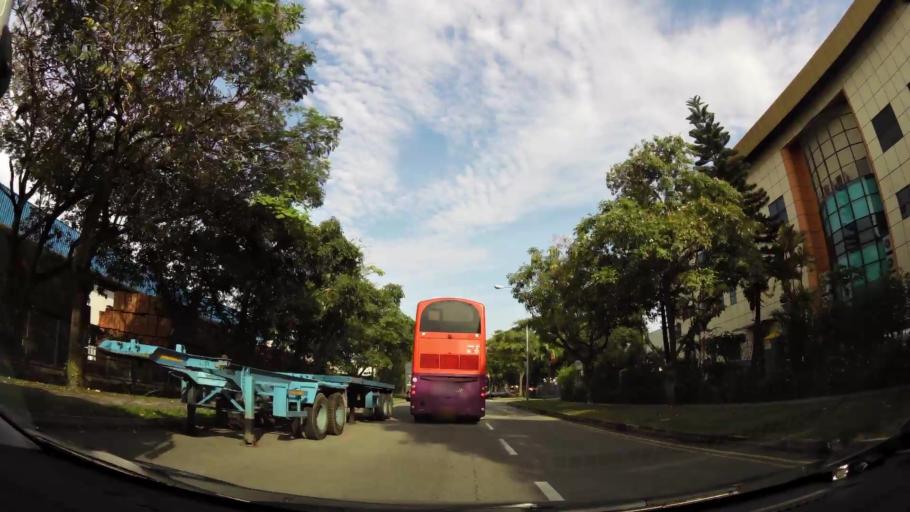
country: MY
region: Johor
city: Johor Bahru
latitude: 1.3332
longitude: 103.6489
